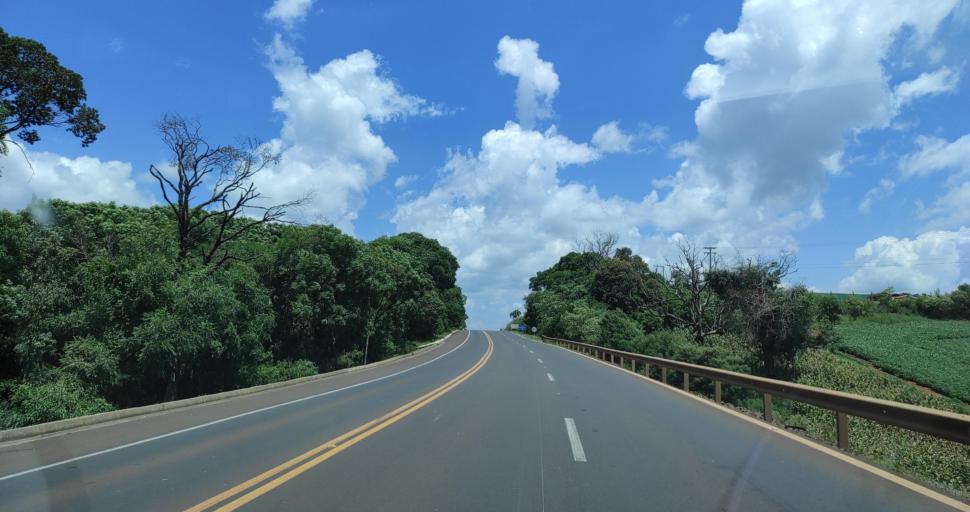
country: BR
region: Santa Catarina
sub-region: Xanxere
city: Xanxere
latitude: -26.8790
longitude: -52.3510
